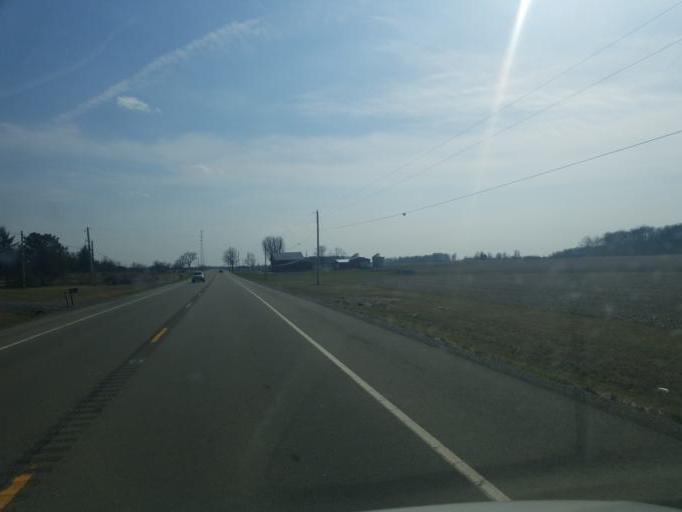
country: US
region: Ohio
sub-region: Logan County
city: Northwood
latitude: 40.5232
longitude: -83.6844
